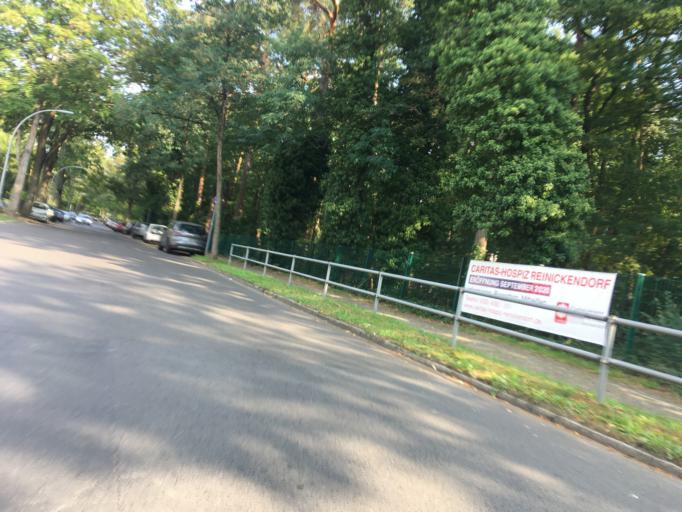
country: DE
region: Berlin
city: Frohnau
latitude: 52.6258
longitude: 13.2915
